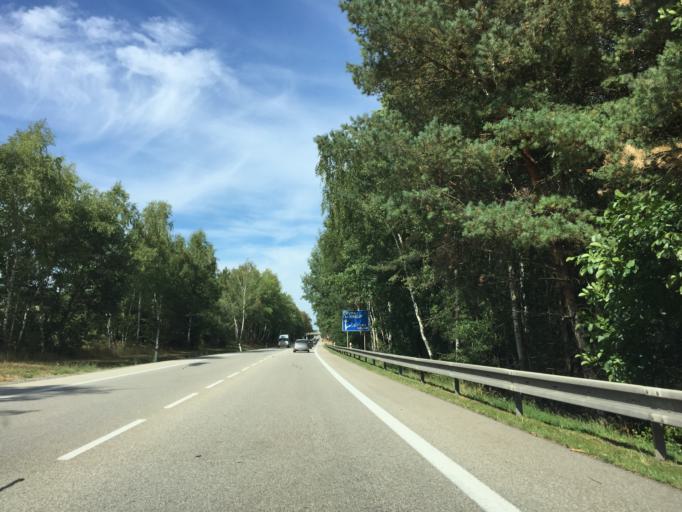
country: CZ
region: Central Bohemia
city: Votice
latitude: 49.6561
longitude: 14.6331
